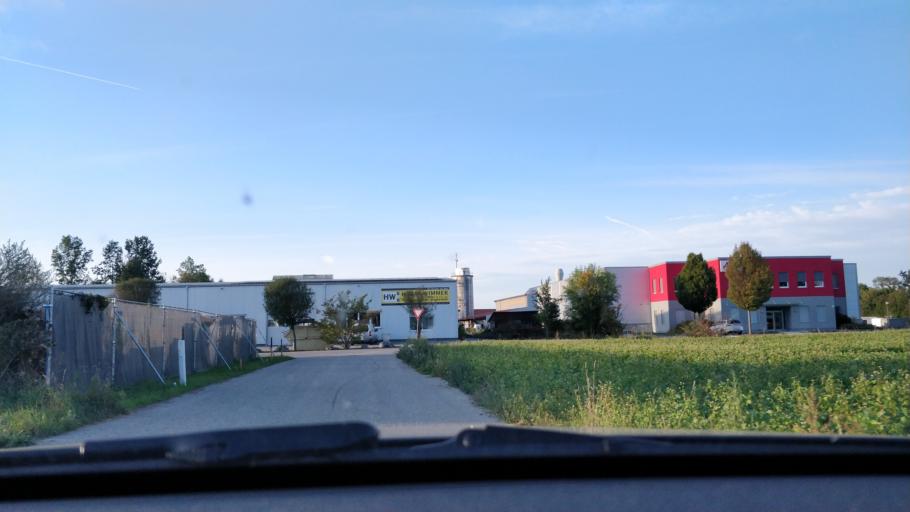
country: AT
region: Upper Austria
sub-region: Politischer Bezirk Braunau am Inn
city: Braunau am Inn
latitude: 48.1672
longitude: 13.1229
